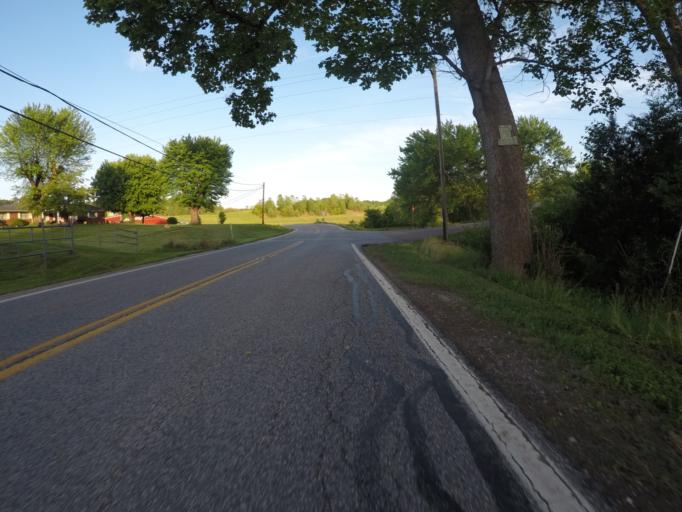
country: US
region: West Virginia
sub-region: Cabell County
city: Huntington
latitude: 38.4865
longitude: -82.4688
